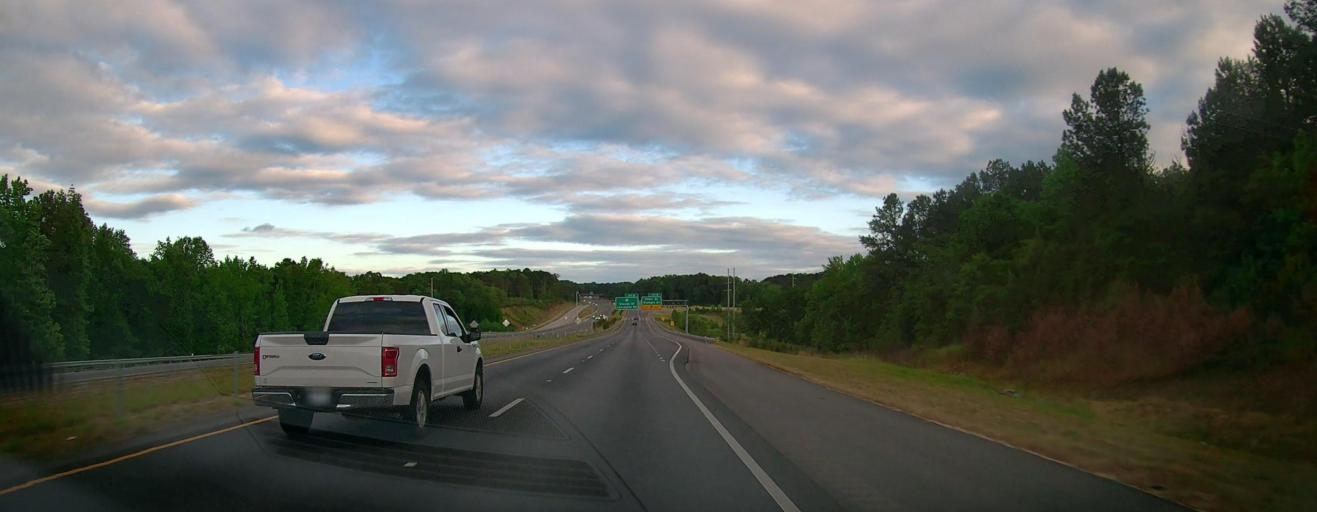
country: US
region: Georgia
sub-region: Clarke County
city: Athens
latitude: 33.9676
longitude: -83.3540
